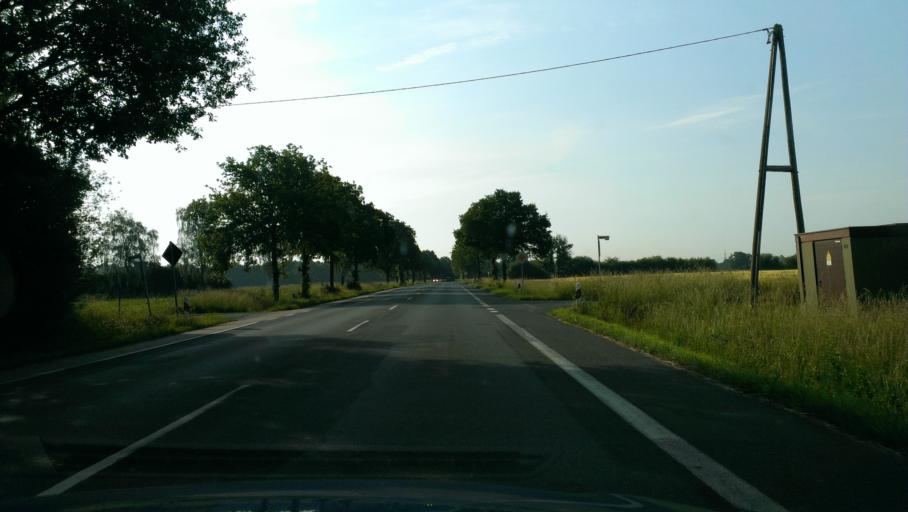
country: DE
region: North Rhine-Westphalia
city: Ahlen
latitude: 51.8148
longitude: 7.9305
